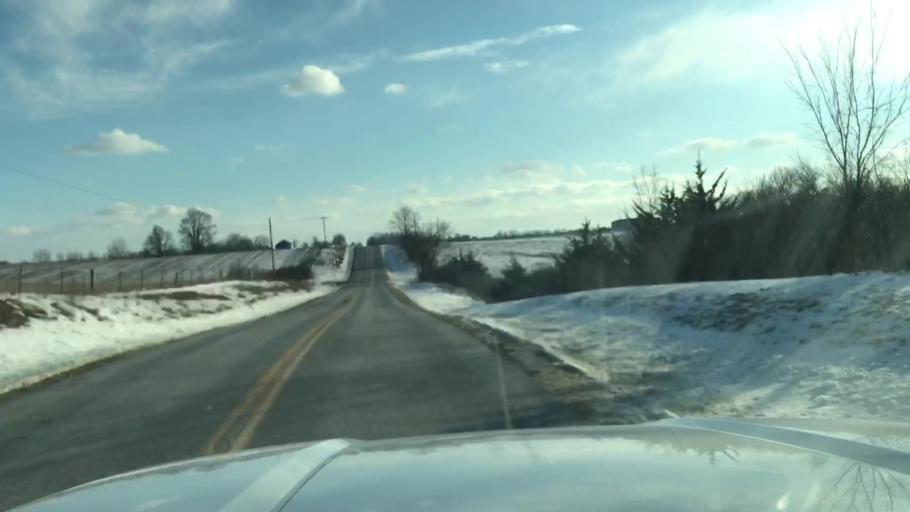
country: US
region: Missouri
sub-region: Holt County
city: Oregon
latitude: 40.0643
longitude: -94.9748
